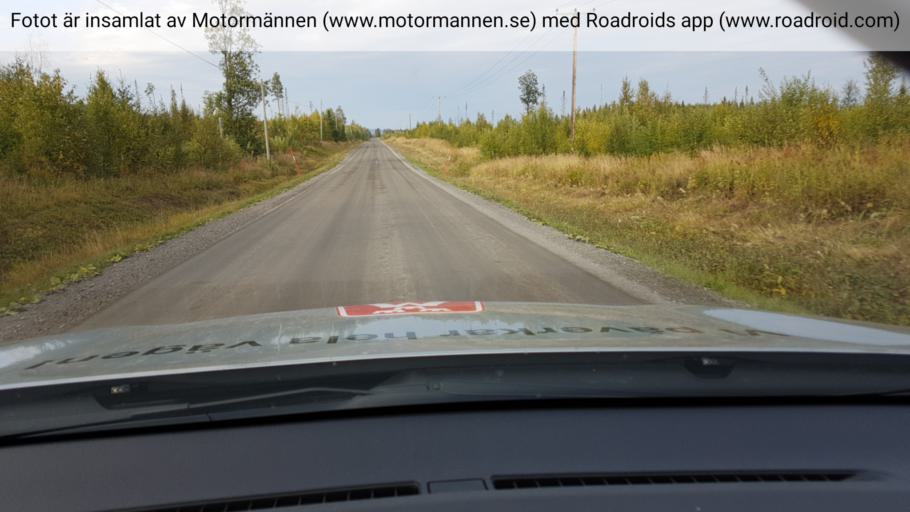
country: SE
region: Jaemtland
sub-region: Stroemsunds Kommun
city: Stroemsund
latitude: 63.9866
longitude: 15.8163
